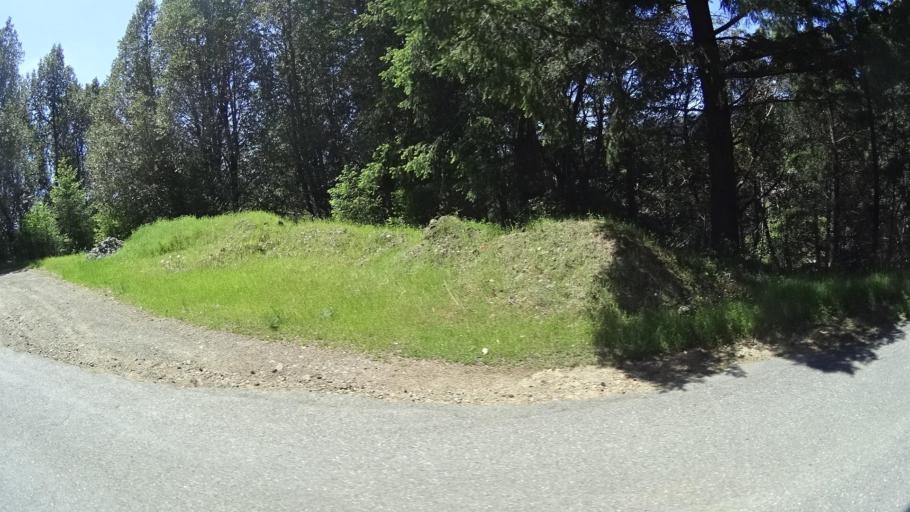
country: US
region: California
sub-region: Humboldt County
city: Rio Dell
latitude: 40.2552
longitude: -124.1194
